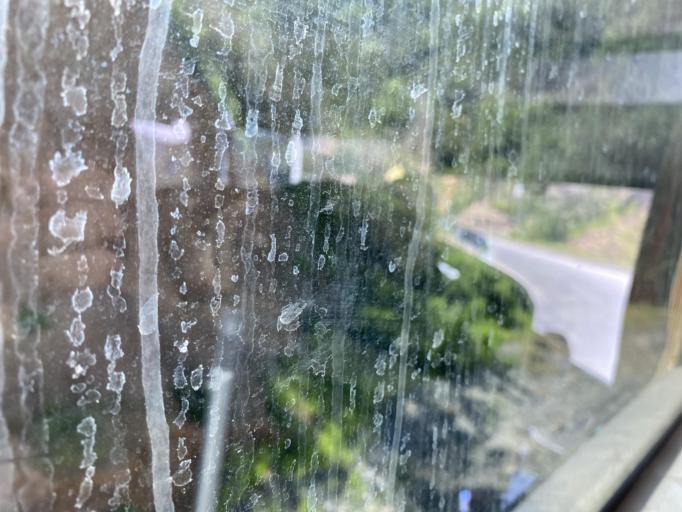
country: CL
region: Valparaiso
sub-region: Provincia de Marga Marga
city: Limache
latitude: -33.1984
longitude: -71.2673
